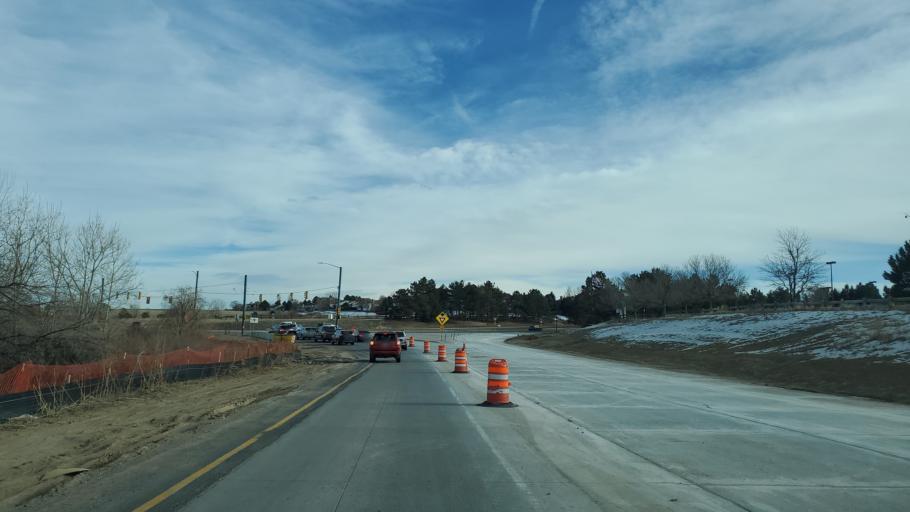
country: US
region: Colorado
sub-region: Douglas County
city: Highlands Ranch
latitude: 39.5626
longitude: -104.9620
